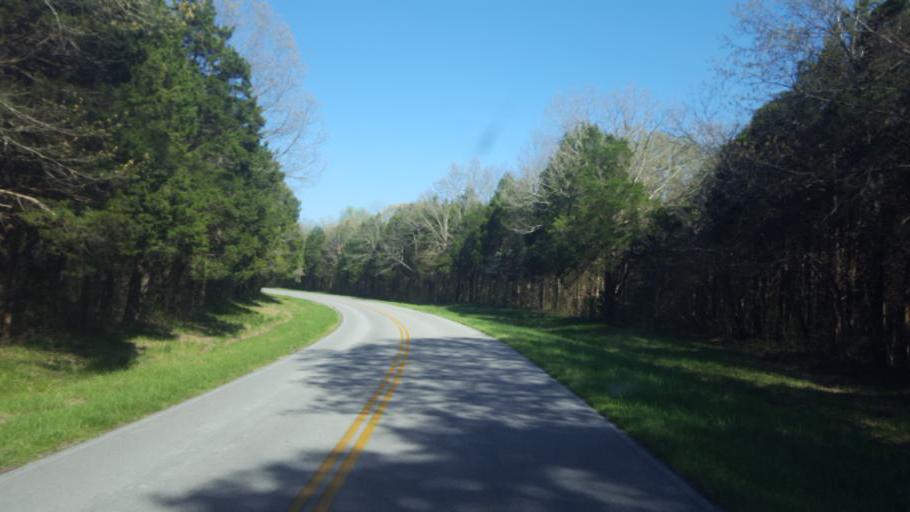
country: US
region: Kentucky
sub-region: Edmonson County
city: Brownsville
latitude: 37.1499
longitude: -86.1171
